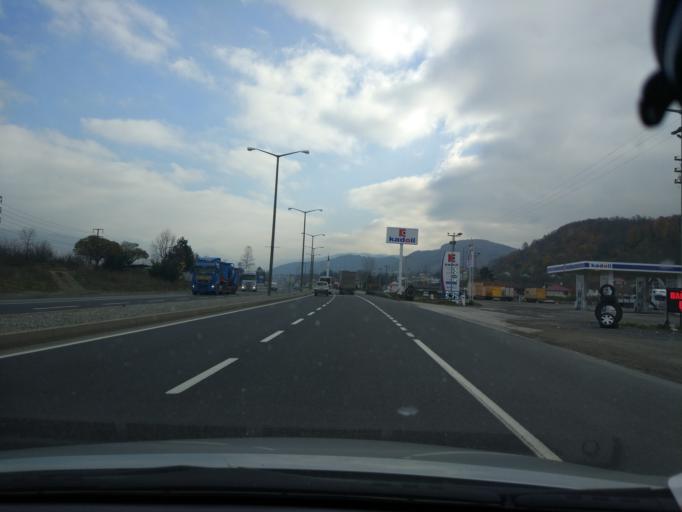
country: TR
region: Duzce
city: Kaynasli
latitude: 40.7796
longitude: 31.2841
